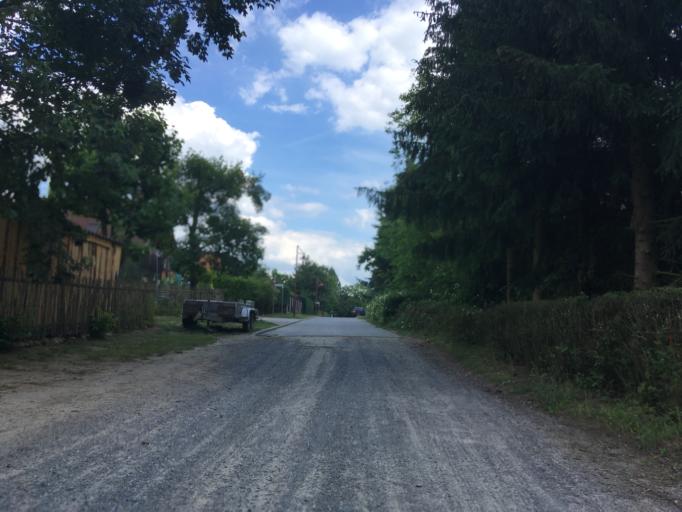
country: DE
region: Brandenburg
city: Muncheberg
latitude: 52.5119
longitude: 14.1059
